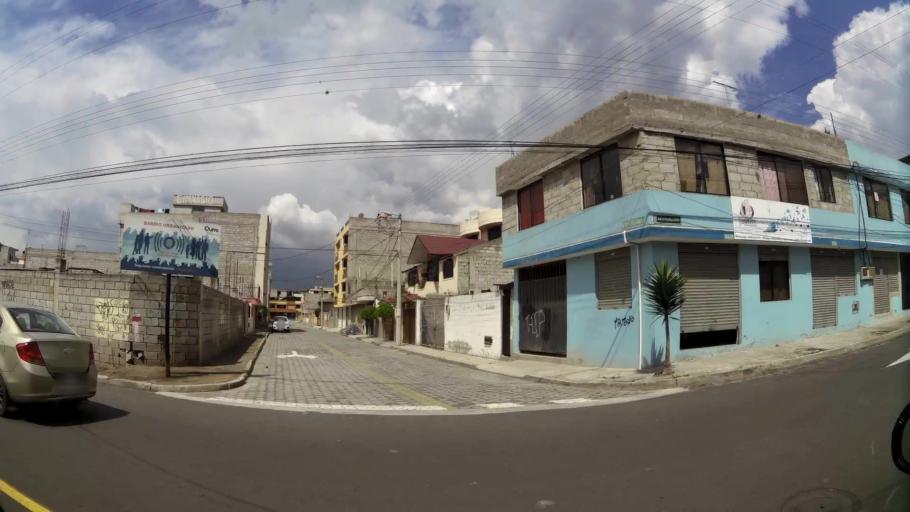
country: EC
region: Pichincha
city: Quito
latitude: -0.0999
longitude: -78.4552
